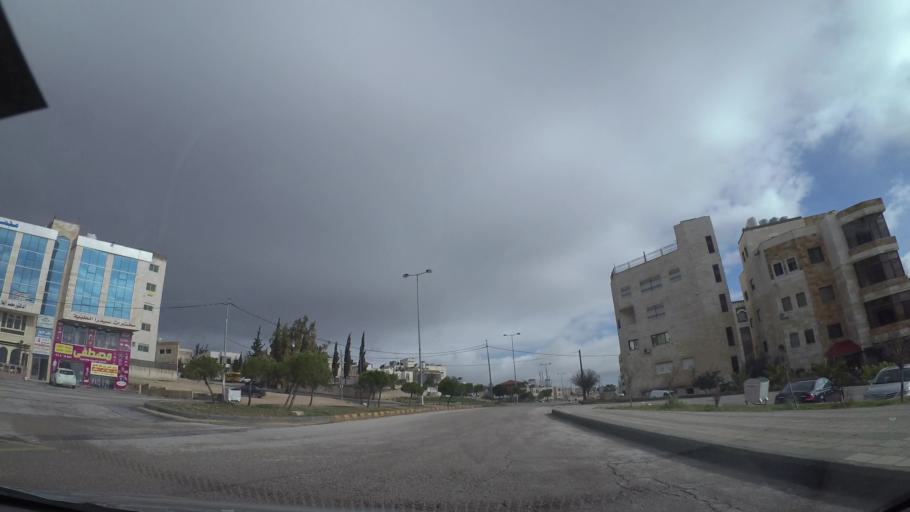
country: JO
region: Amman
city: Al Jubayhah
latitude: 32.0509
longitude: 35.8851
